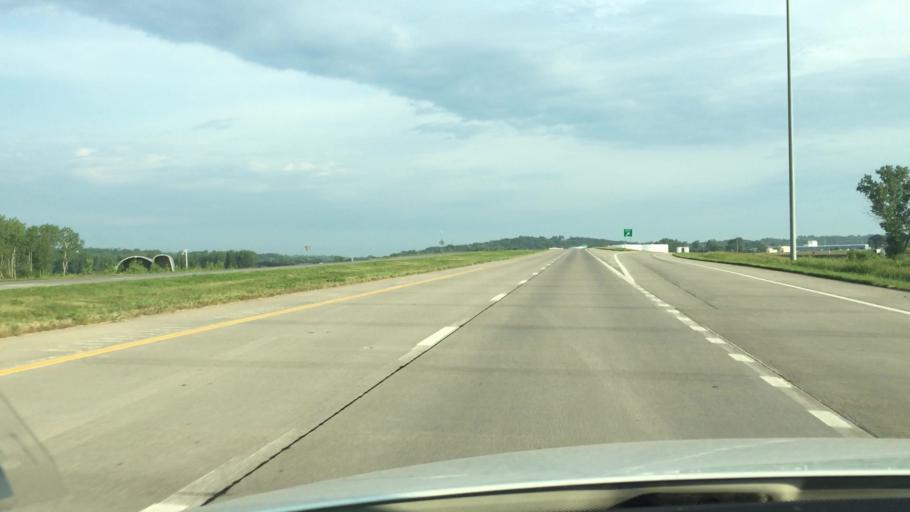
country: US
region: Kansas
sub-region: Doniphan County
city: Wathena
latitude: 39.7441
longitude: -94.9215
